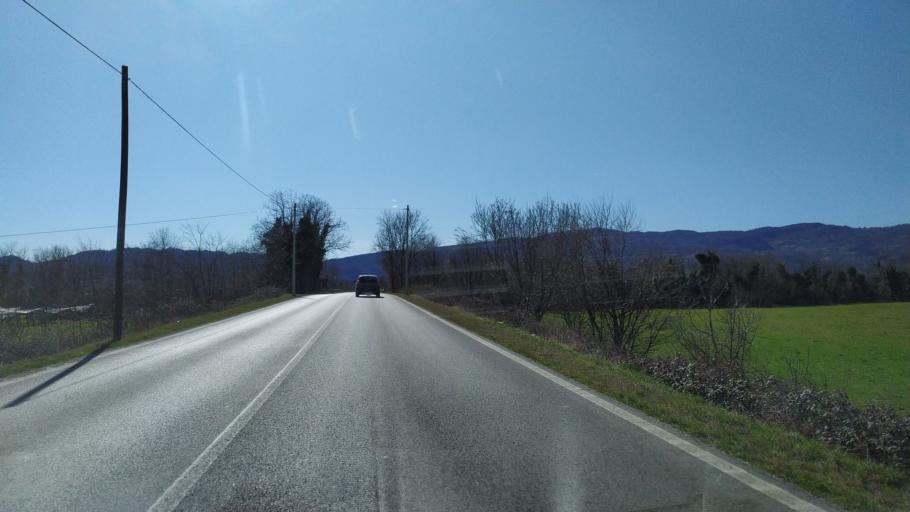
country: IT
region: Veneto
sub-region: Provincia di Vicenza
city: Giavenale
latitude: 45.6858
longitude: 11.4113
